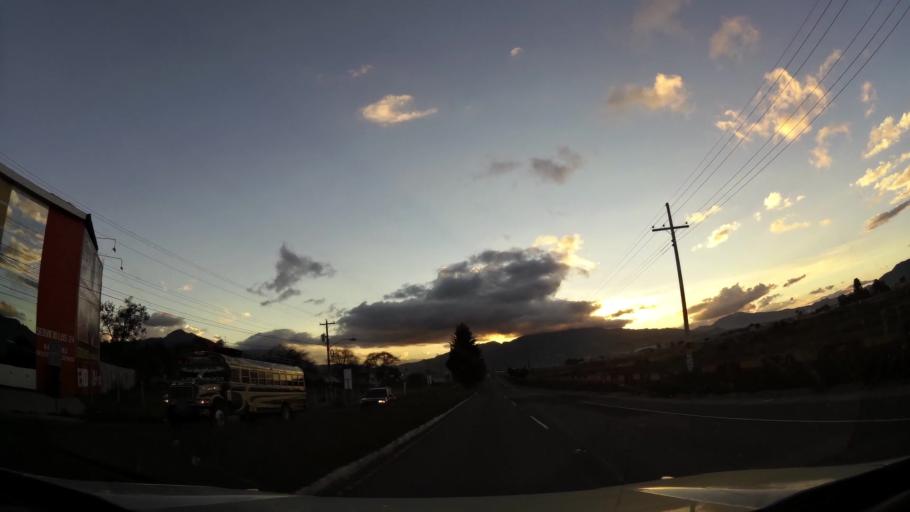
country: GT
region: Quetzaltenango
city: Olintepeque
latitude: 14.8646
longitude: -91.5018
